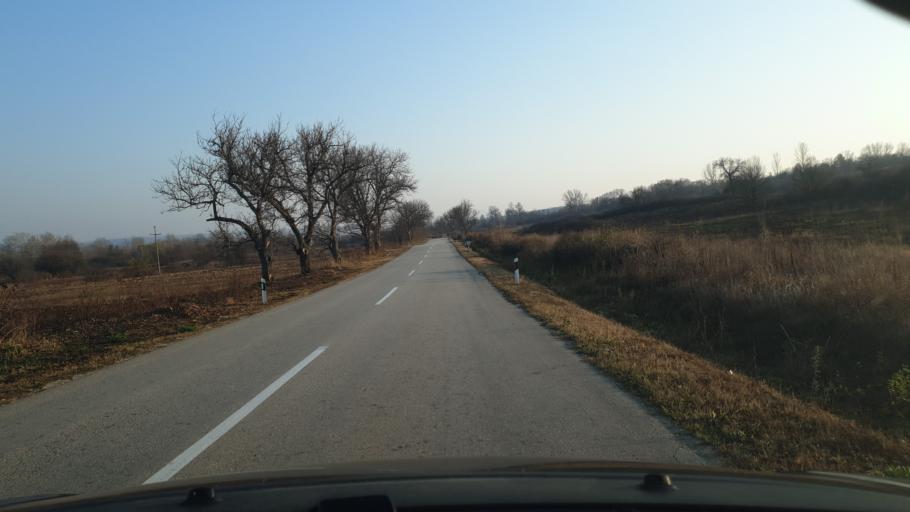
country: RS
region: Central Serbia
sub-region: Zajecarski Okrug
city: Zajecar
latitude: 43.9860
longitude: 22.2863
